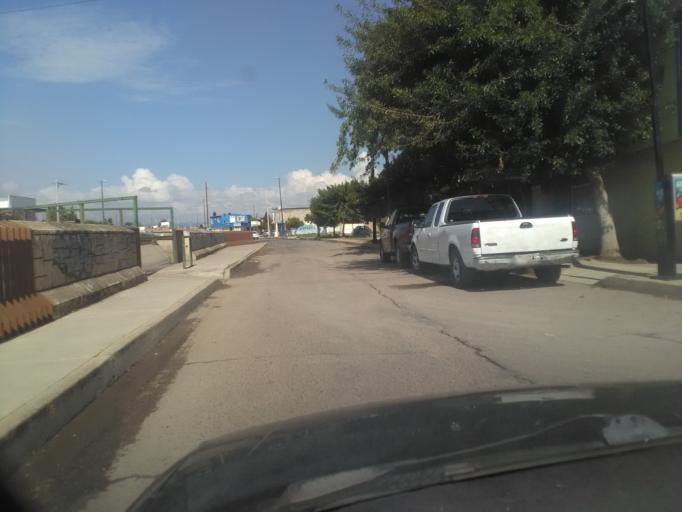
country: MX
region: Durango
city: Victoria de Durango
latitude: 24.0183
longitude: -104.6309
